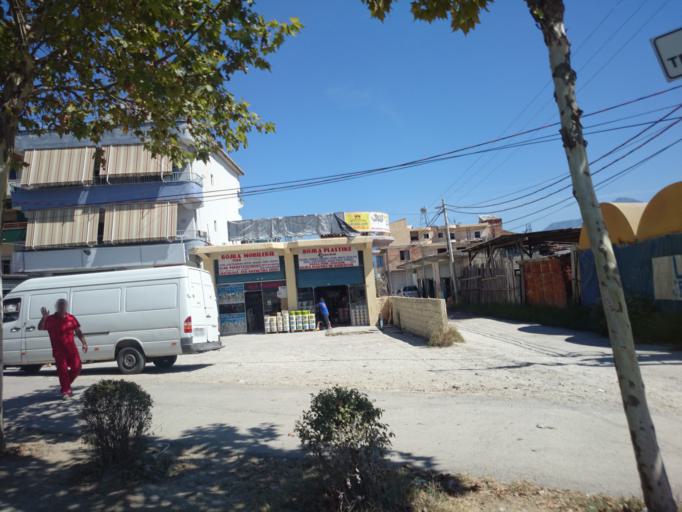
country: AL
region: Tirane
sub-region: Rrethi i Tiranes
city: Paskuqan
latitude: 41.3299
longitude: 19.7852
